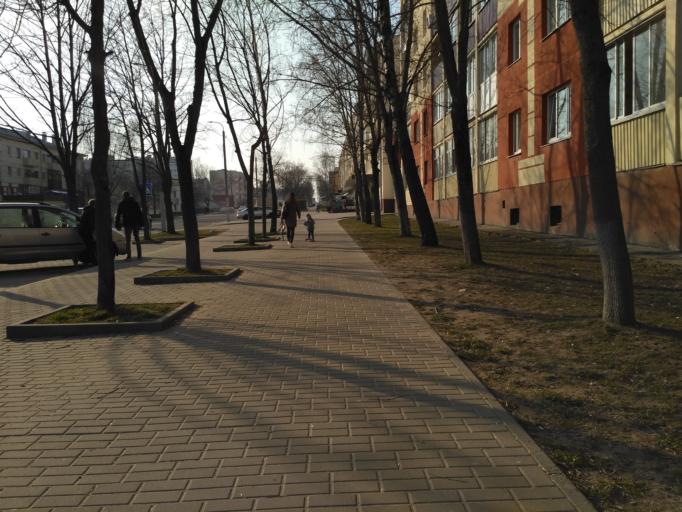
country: BY
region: Minsk
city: Zaslawye
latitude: 54.0106
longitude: 27.2717
